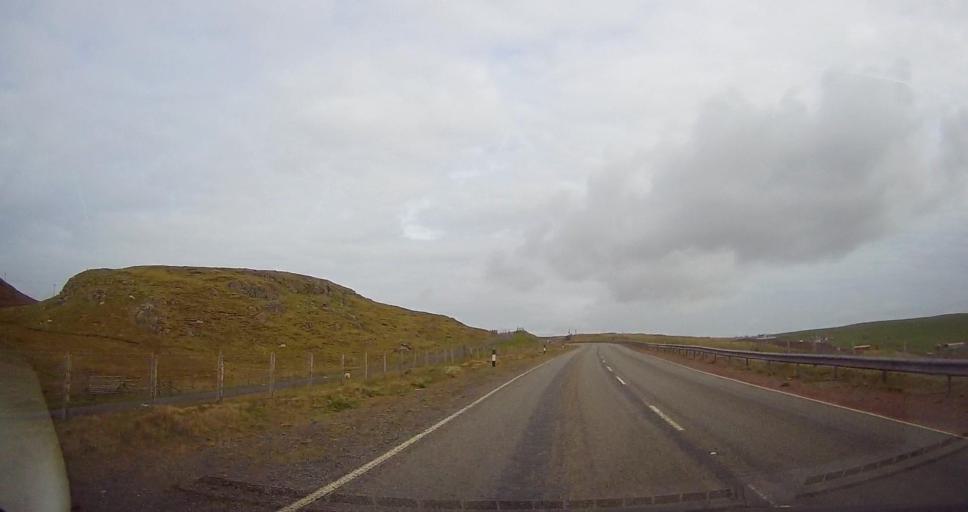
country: GB
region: Scotland
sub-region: Shetland Islands
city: Lerwick
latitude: 60.1088
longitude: -1.2195
